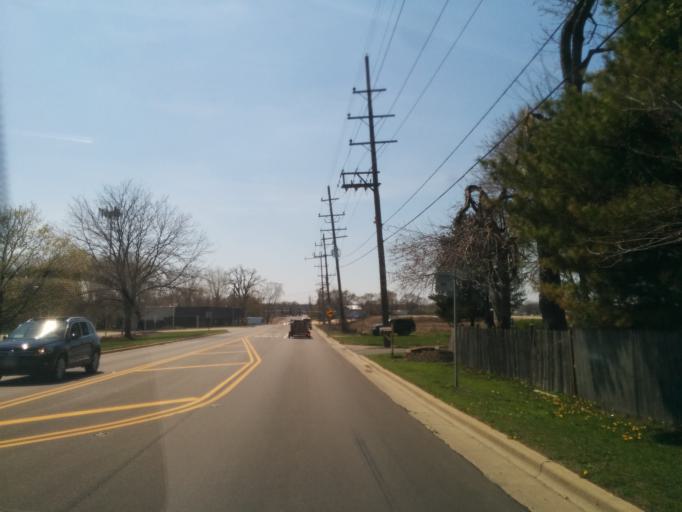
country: US
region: Illinois
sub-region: Kane County
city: South Elgin
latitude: 42.0119
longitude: -88.2881
